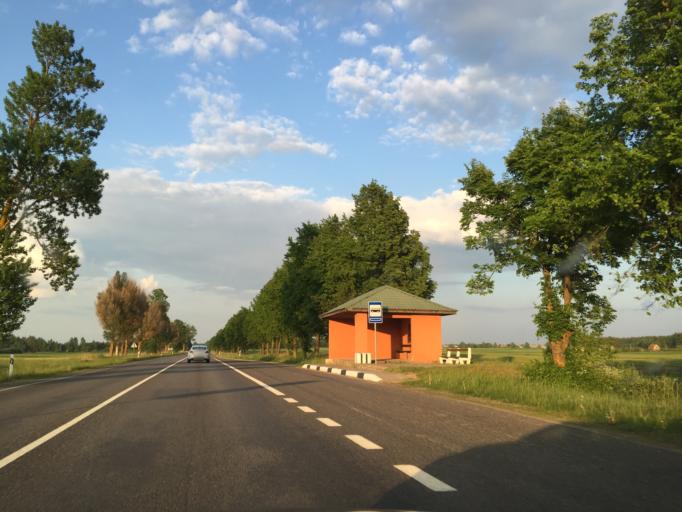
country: LT
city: Kursenai
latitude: 55.9989
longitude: 22.8863
